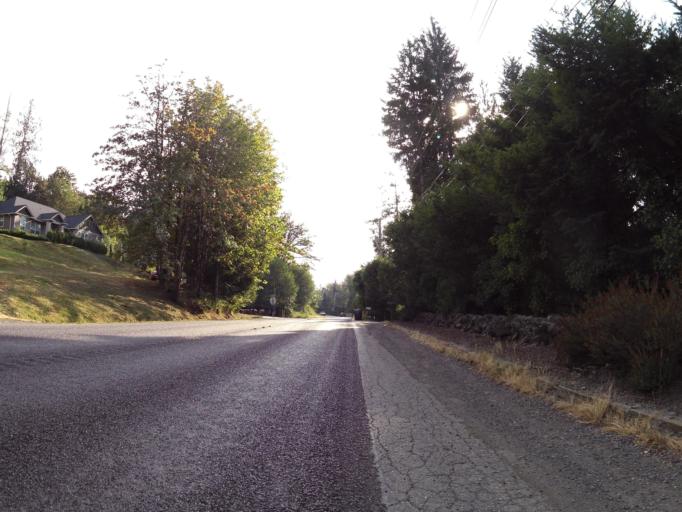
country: US
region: Washington
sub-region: Mason County
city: Belfair
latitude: 47.4238
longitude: -122.8599
